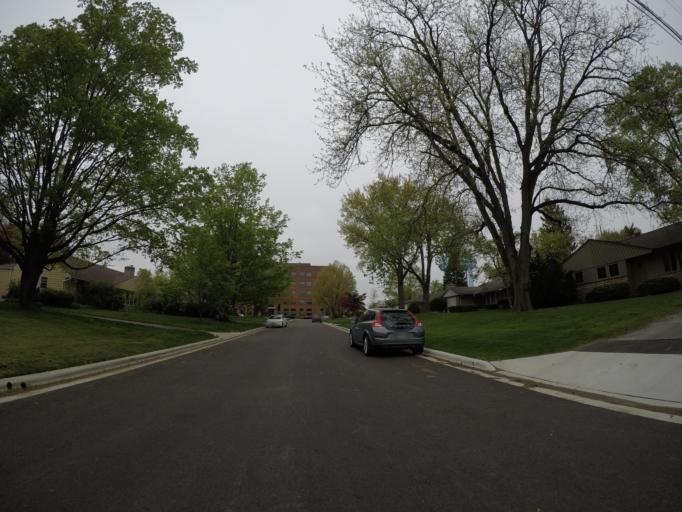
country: US
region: Ohio
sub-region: Franklin County
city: Upper Arlington
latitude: 40.0179
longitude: -83.0609
